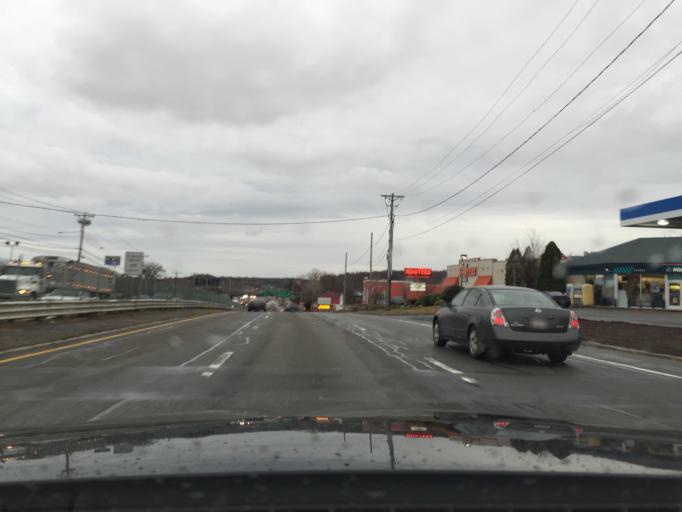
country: US
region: Massachusetts
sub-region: Essex County
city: Saugus
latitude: 42.4678
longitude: -71.0256
